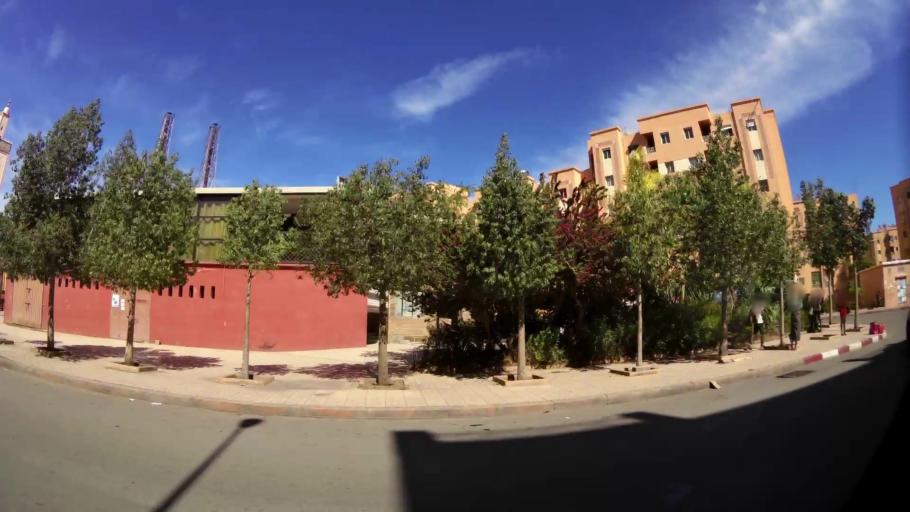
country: MA
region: Marrakech-Tensift-Al Haouz
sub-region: Marrakech
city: Marrakesh
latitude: 31.6748
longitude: -8.0172
